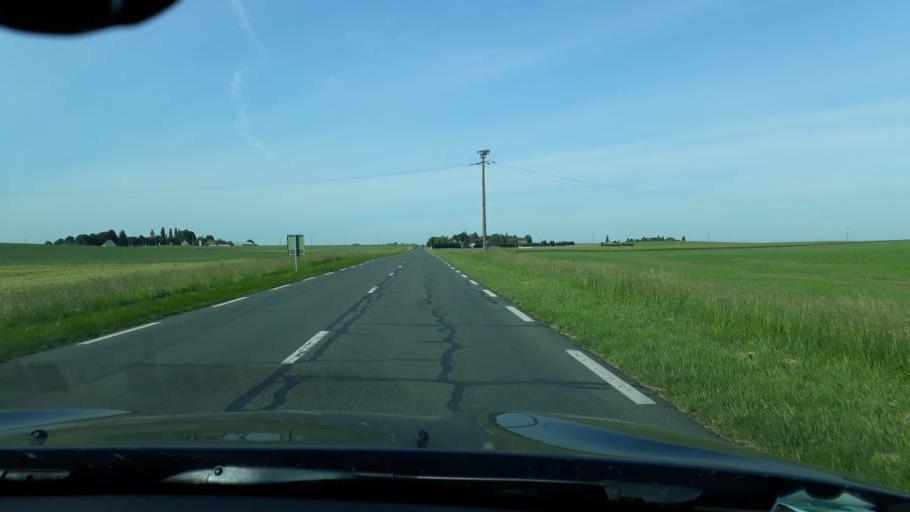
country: FR
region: Centre
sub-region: Departement du Loiret
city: Chilleurs-aux-Bois
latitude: 48.0966
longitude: 2.1611
